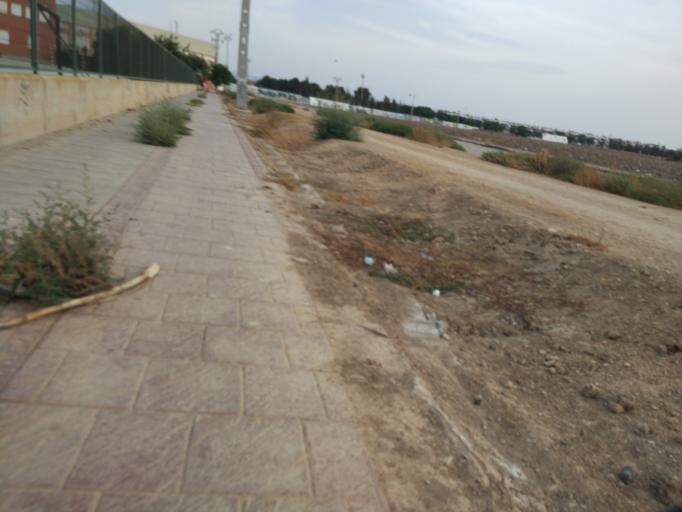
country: ES
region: Murcia
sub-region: Murcia
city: Los Alcazares
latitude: 37.7433
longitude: -0.8583
